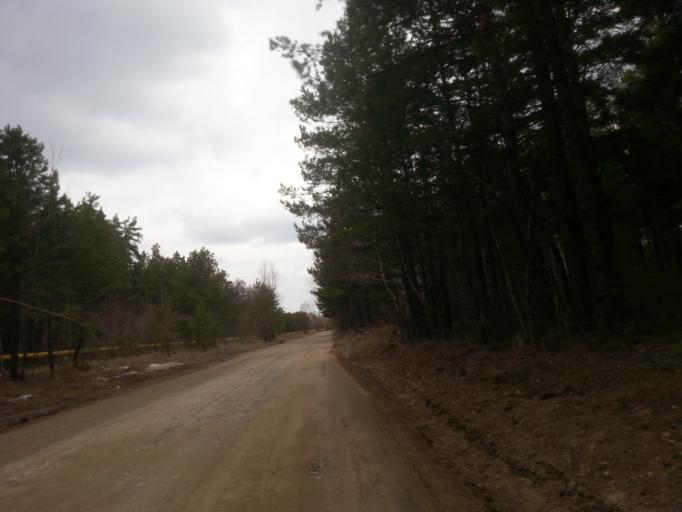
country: RU
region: Altai Krai
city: Yuzhnyy
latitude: 53.2824
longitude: 83.7334
